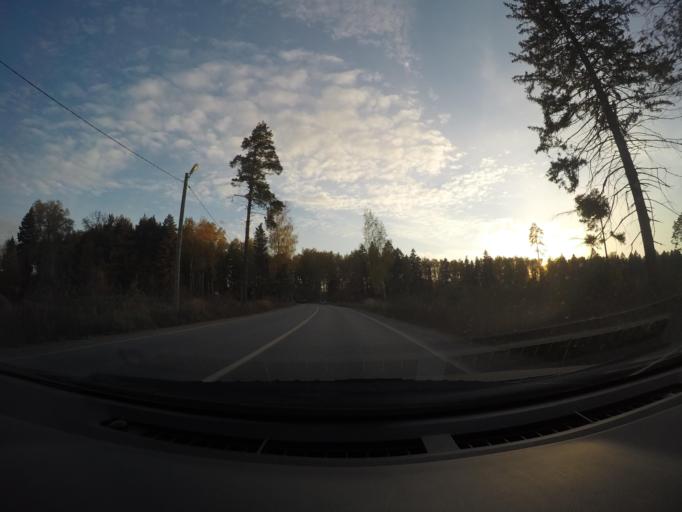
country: RU
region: Moskovskaya
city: Firsanovka
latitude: 55.9623
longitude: 37.2521
